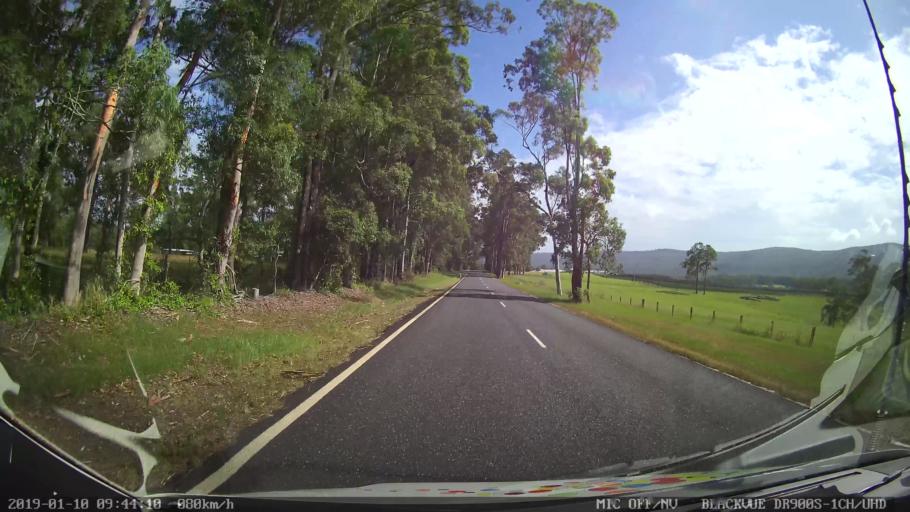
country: AU
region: New South Wales
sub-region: Coffs Harbour
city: Nana Glen
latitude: -30.1200
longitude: 153.0035
